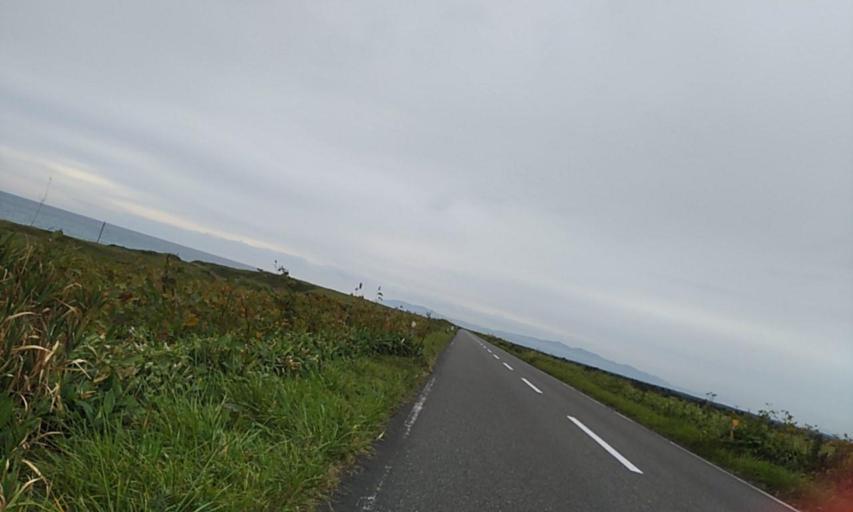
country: JP
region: Hokkaido
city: Makubetsu
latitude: 45.2682
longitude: 142.2390
